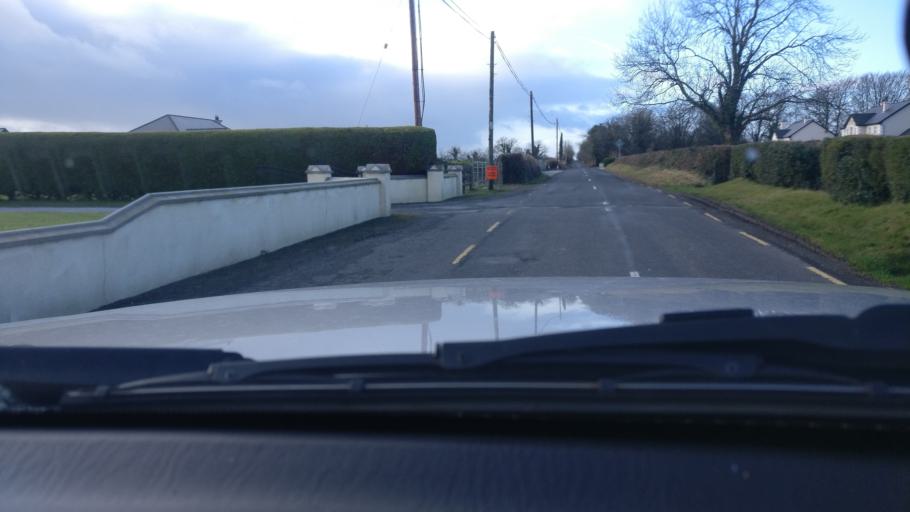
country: IE
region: Connaught
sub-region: County Galway
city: Ballinasloe
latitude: 53.2301
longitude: -8.2976
